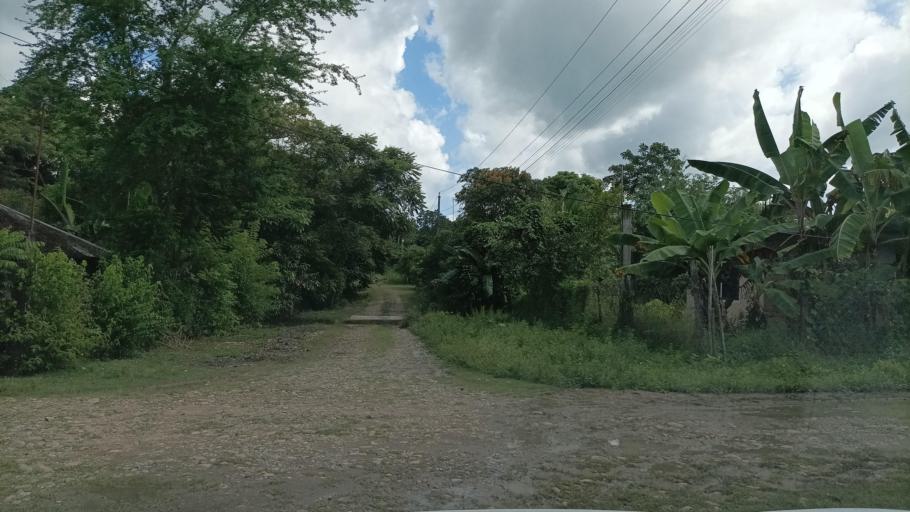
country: MX
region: Veracruz
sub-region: Tantoyuca
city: El Lindero
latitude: 21.1906
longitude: -98.1471
